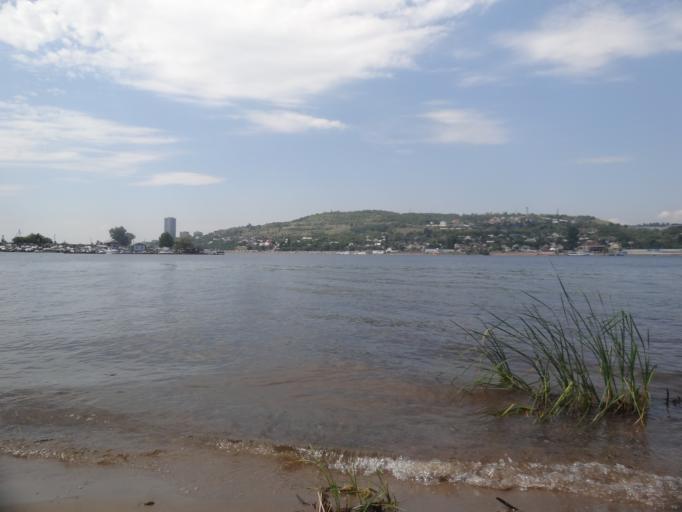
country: RU
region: Saratov
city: Engel's
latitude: 51.5407
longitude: 46.0901
